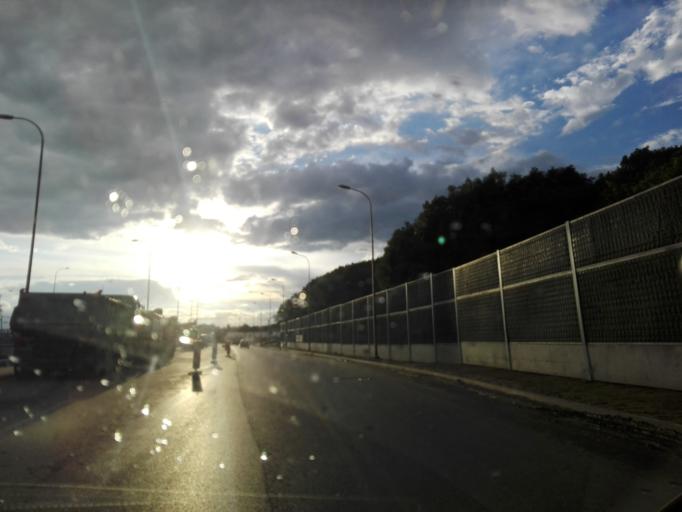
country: PL
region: Lublin Voivodeship
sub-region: Powiat lubelski
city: Lublin
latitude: 51.2578
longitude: 22.5361
